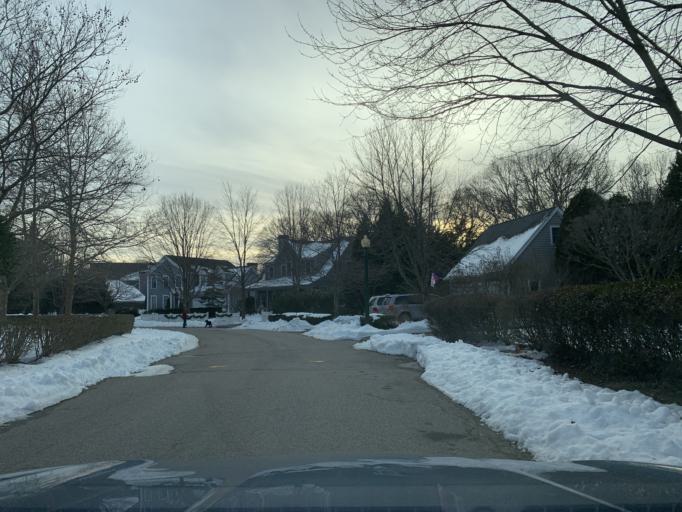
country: US
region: Rhode Island
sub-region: Washington County
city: North Kingstown
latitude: 41.5851
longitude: -71.4476
